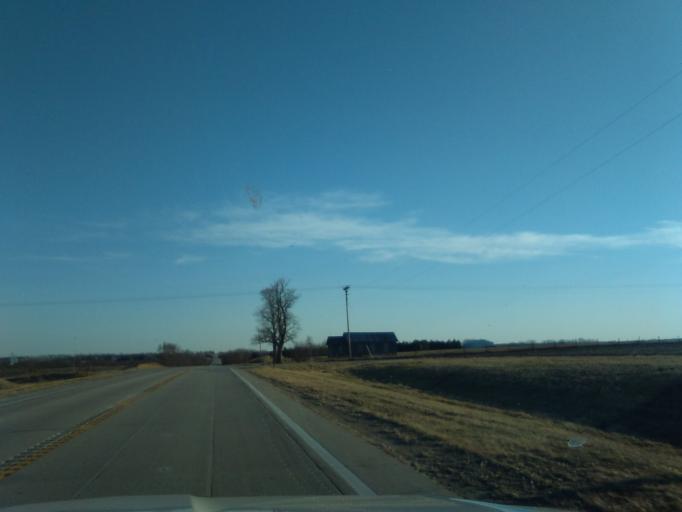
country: US
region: Nebraska
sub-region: Johnson County
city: Tecumseh
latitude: 40.4804
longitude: -96.1799
